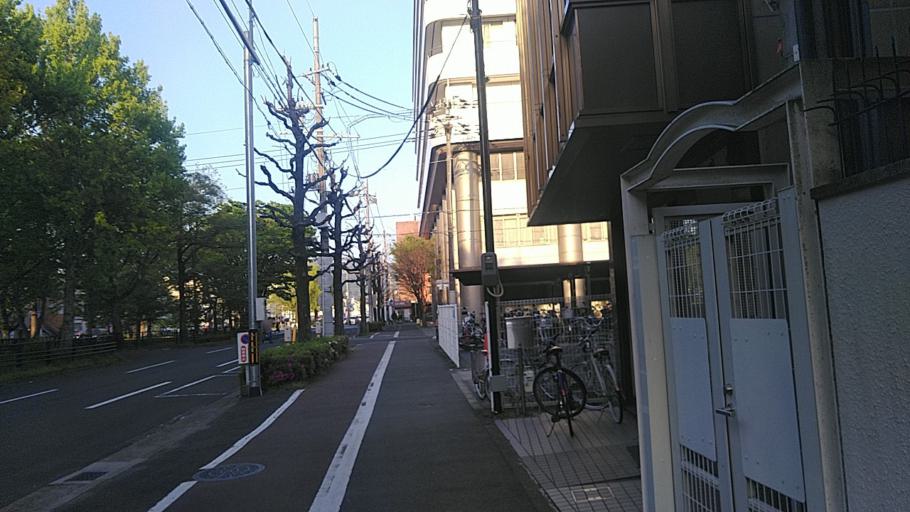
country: JP
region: Kyoto
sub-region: Kyoto-shi
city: Kamigyo-ku
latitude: 35.0397
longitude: 135.7580
